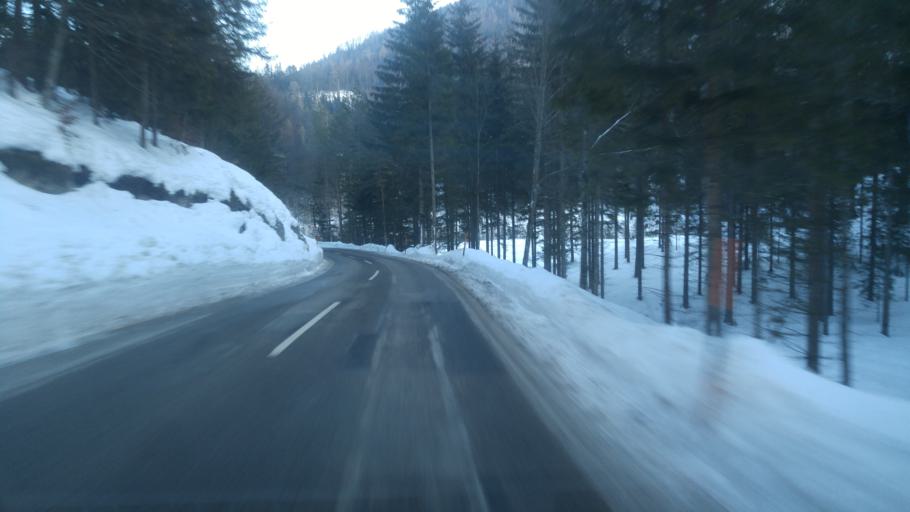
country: AT
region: Lower Austria
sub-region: Politischer Bezirk Lilienfeld
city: Hohenberg
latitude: 47.8879
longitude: 15.6647
